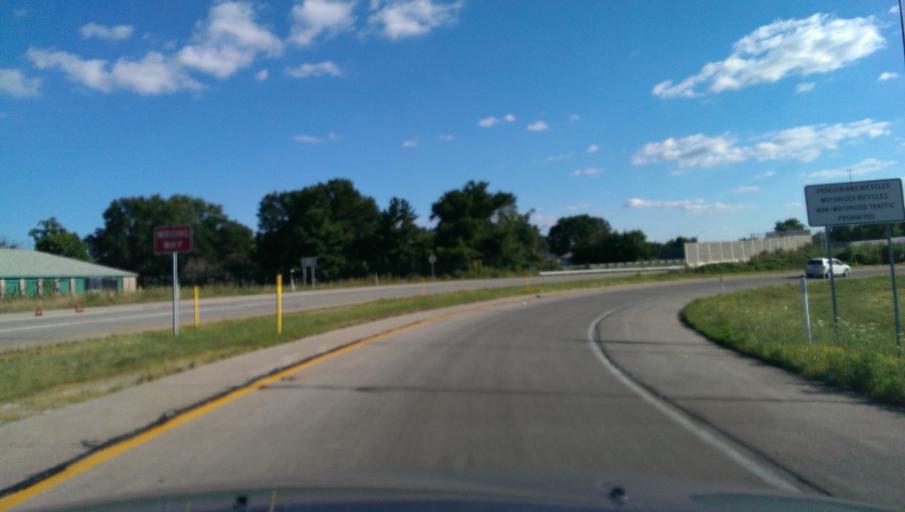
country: US
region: Indiana
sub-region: Marion County
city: Lawrence
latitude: 39.8544
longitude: -86.0451
